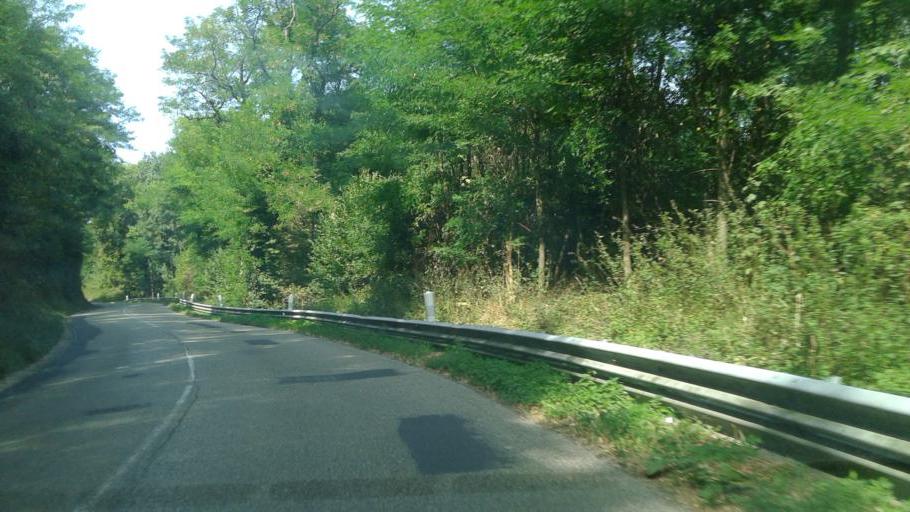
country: FR
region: Rhone-Alpes
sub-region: Departement de l'Ain
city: La Boisse
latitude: 45.8537
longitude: 5.0245
